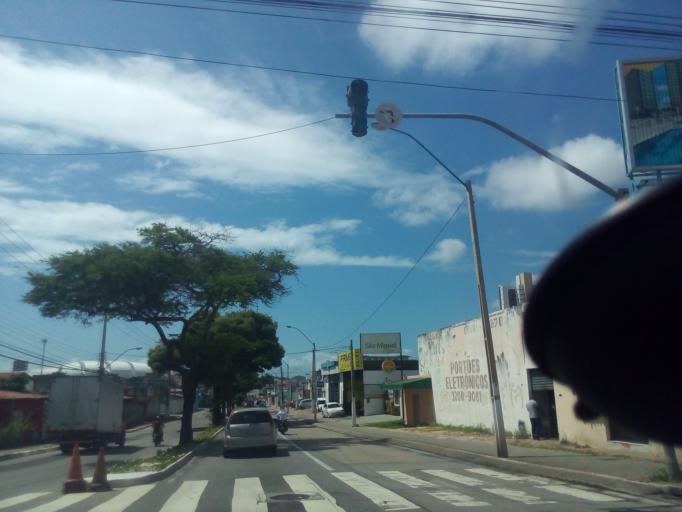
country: BR
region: Rio Grande do Norte
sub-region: Natal
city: Natal
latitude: -5.8258
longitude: -35.2209
